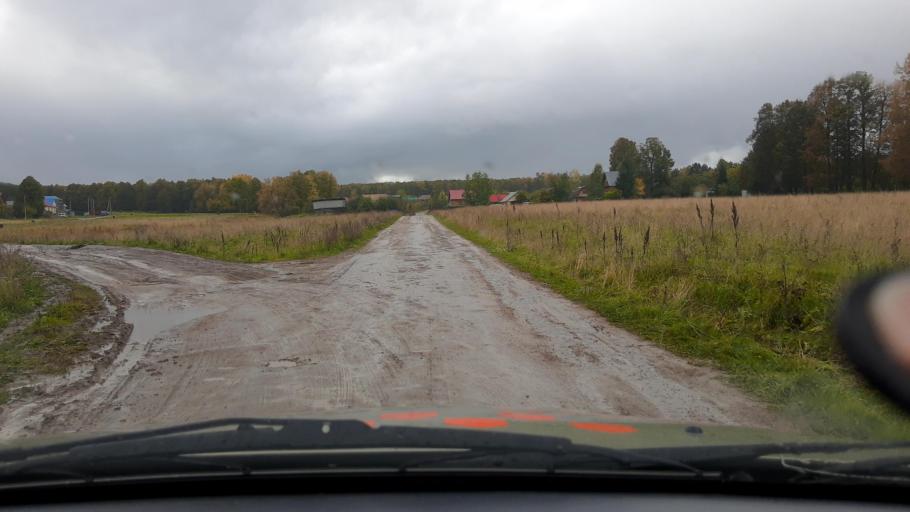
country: RU
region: Bashkortostan
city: Kudeyevskiy
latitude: 54.8774
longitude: 56.6288
